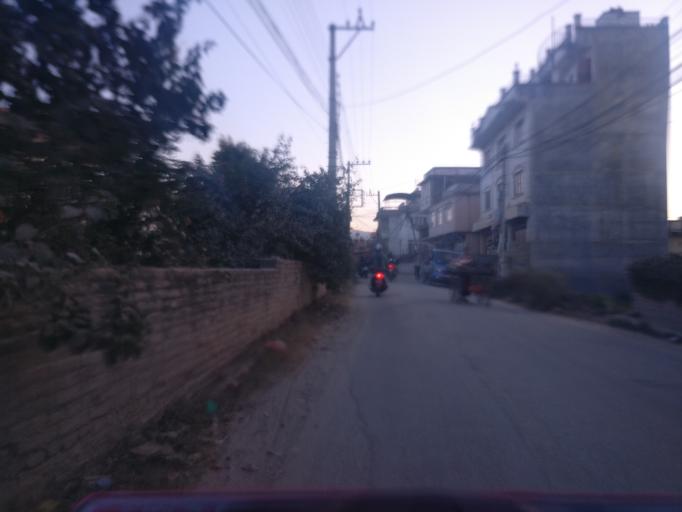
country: NP
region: Central Region
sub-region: Bagmati Zone
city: Patan
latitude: 27.6562
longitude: 85.3171
